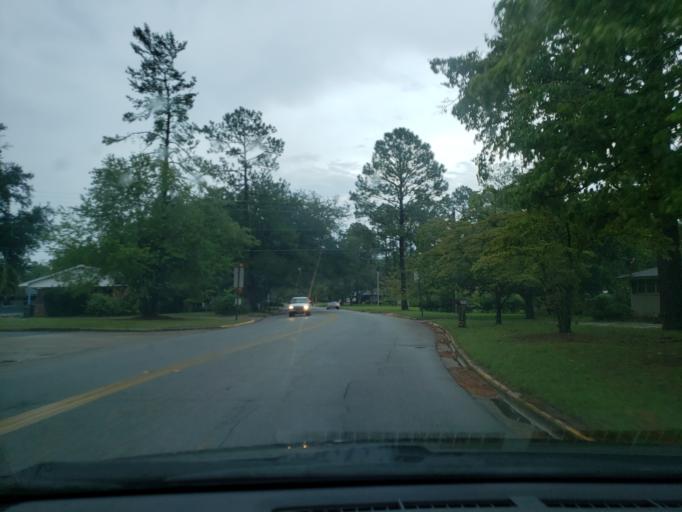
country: US
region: Georgia
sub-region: Dougherty County
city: Albany
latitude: 31.6058
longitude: -84.1979
